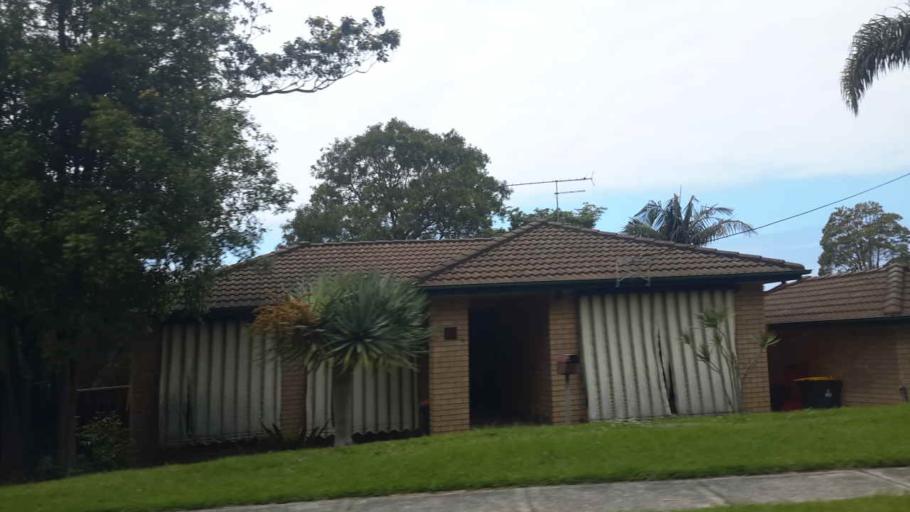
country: AU
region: New South Wales
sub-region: Wollongong
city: Bulli
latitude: -34.3545
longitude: 150.9013
